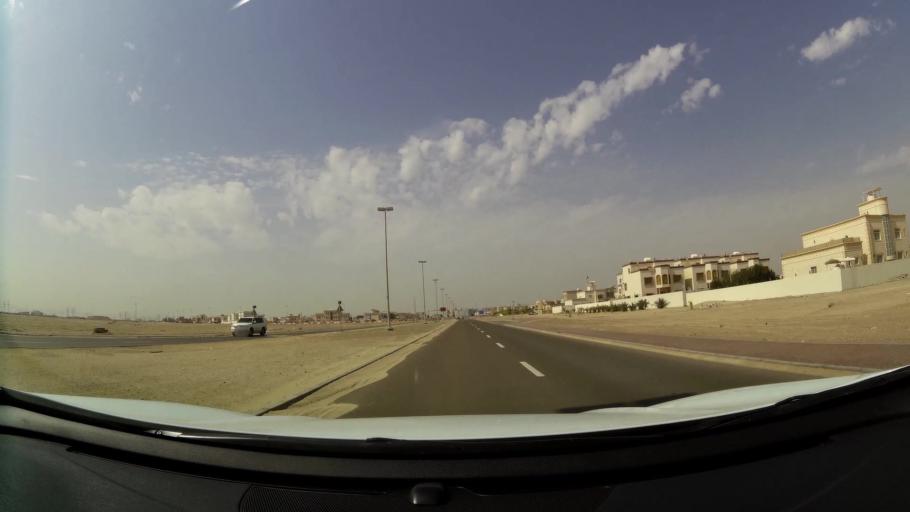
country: AE
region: Abu Dhabi
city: Abu Dhabi
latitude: 24.3045
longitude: 54.5526
